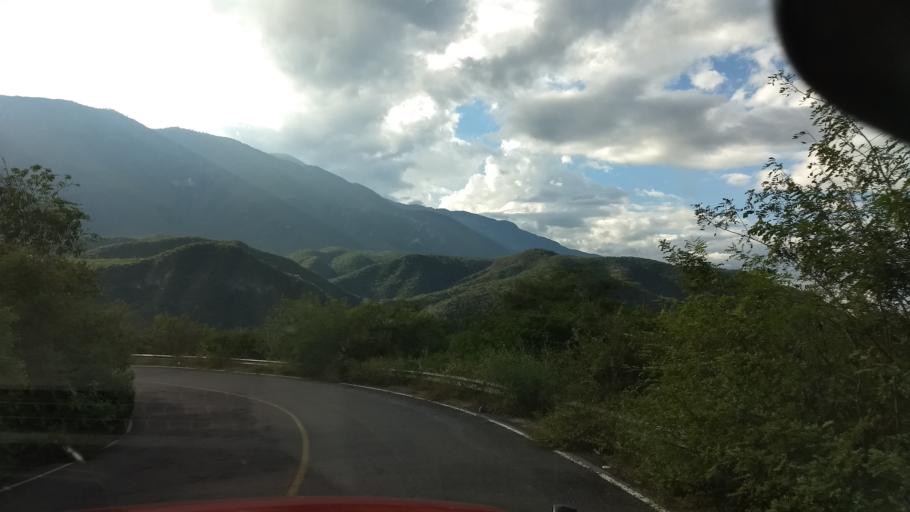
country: MX
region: Colima
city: Suchitlan
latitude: 19.4589
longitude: -103.8219
